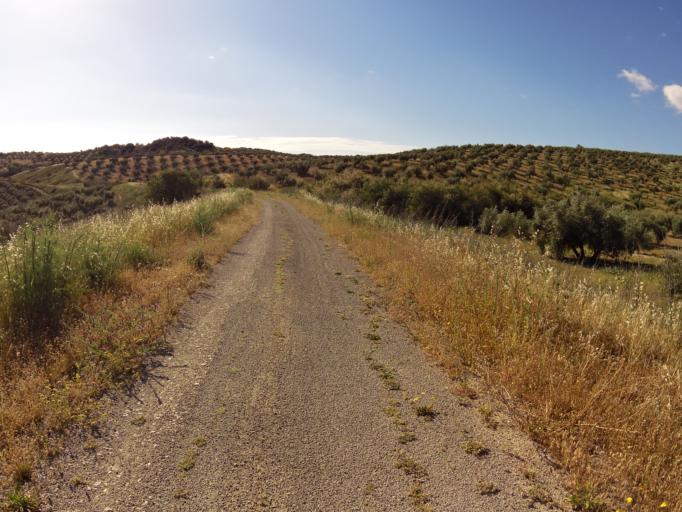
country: ES
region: Andalusia
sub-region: Province of Cordoba
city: Fuente-Tojar
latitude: 37.5790
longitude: -4.1837
